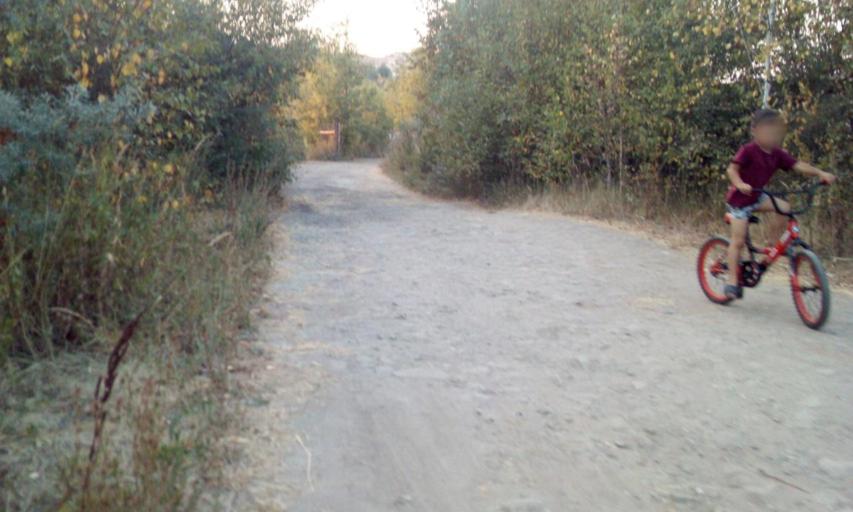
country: RU
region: Moscow
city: Nikulino
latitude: 55.6613
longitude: 37.4617
